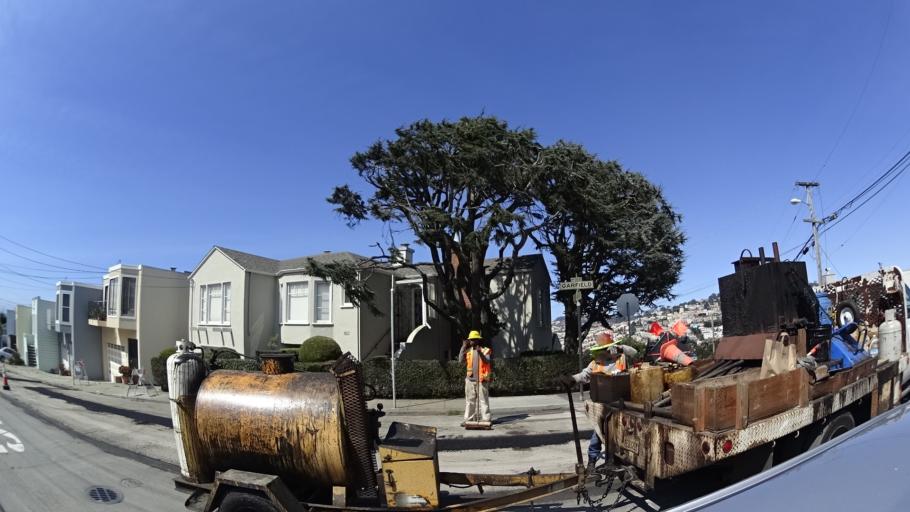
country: US
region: California
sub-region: San Mateo County
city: Daly City
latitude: 37.7199
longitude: -122.4636
